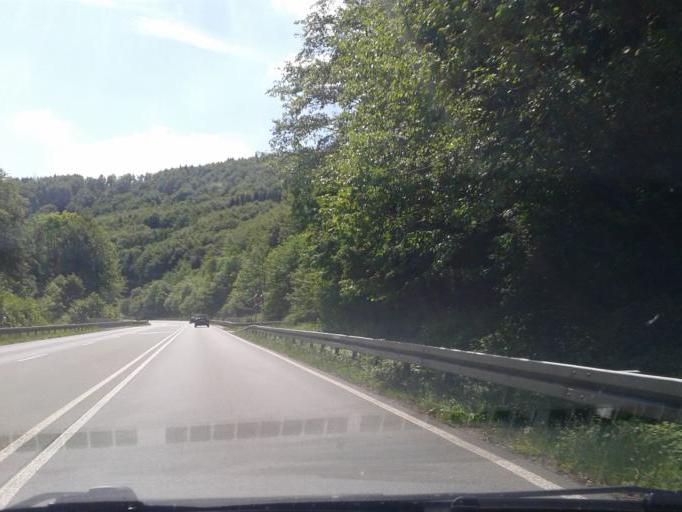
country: DE
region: North Rhine-Westphalia
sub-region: Regierungsbezirk Detmold
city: Horn
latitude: 51.8497
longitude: 8.9135
